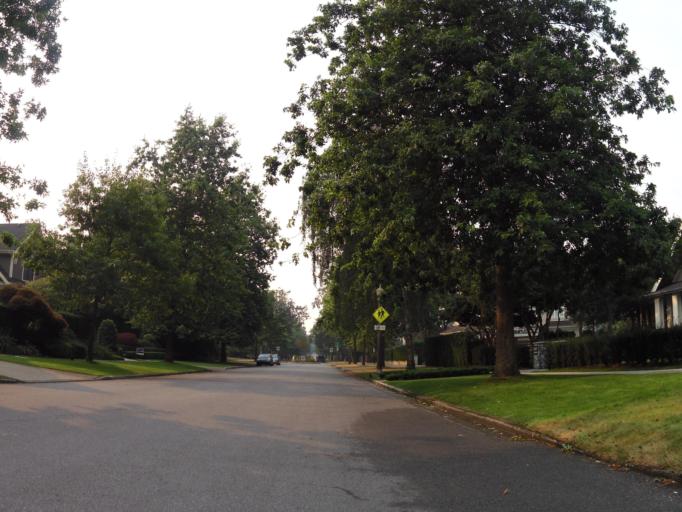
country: CA
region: British Columbia
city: Vancouver
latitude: 49.2315
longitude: -123.1478
